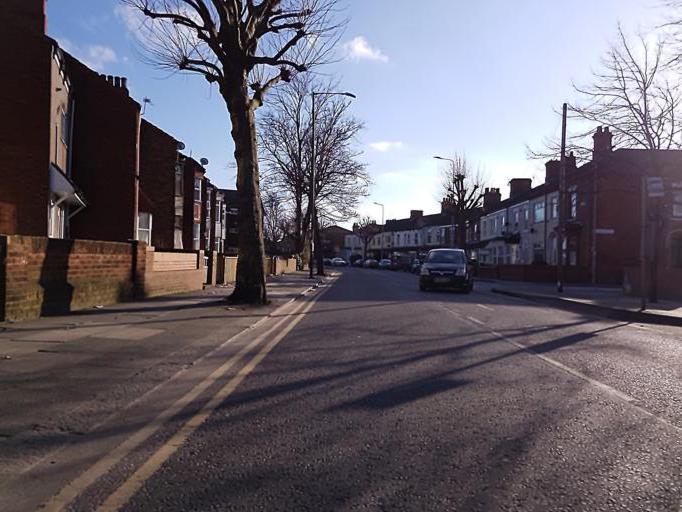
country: GB
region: England
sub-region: North East Lincolnshire
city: Grimsby
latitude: 53.5605
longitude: -0.0765
